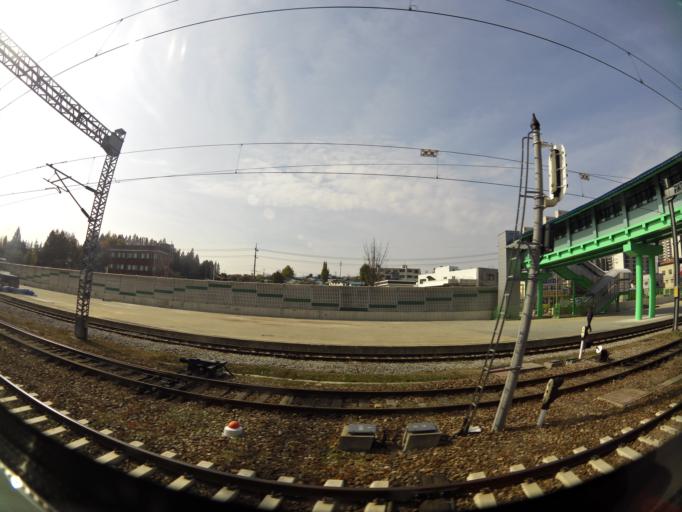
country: KR
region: Daejeon
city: Songgang-dong
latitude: 36.6006
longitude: 127.2956
